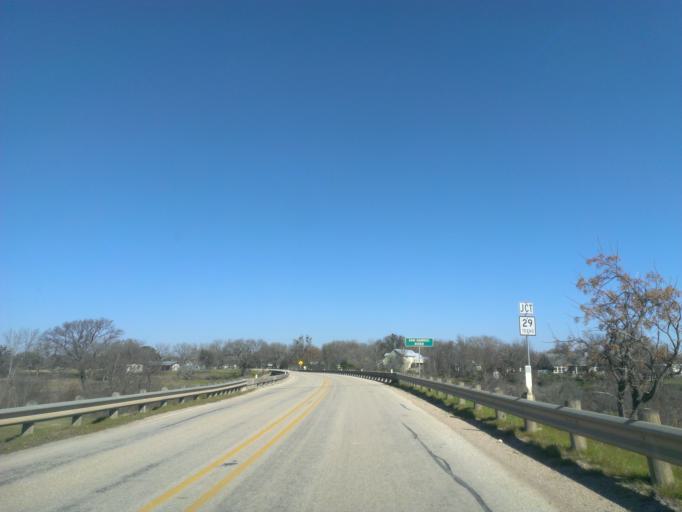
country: US
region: Texas
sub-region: Williamson County
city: Hutto
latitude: 30.6345
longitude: -97.5425
